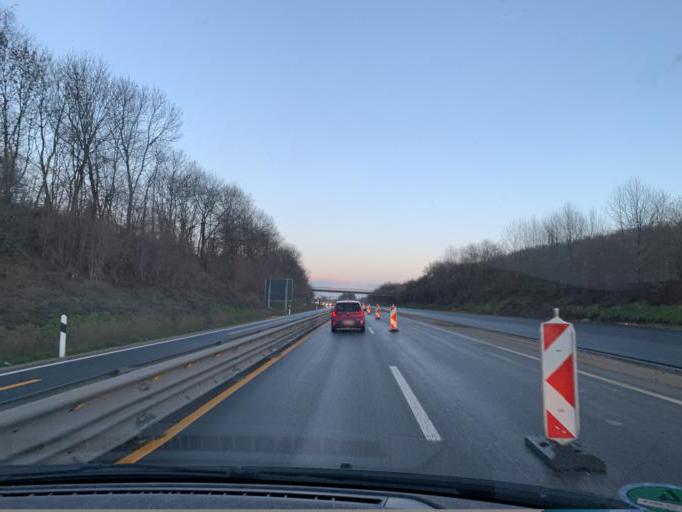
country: DE
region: North Rhine-Westphalia
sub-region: Regierungsbezirk Dusseldorf
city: Grevenbroich
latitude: 51.0752
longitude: 6.5989
